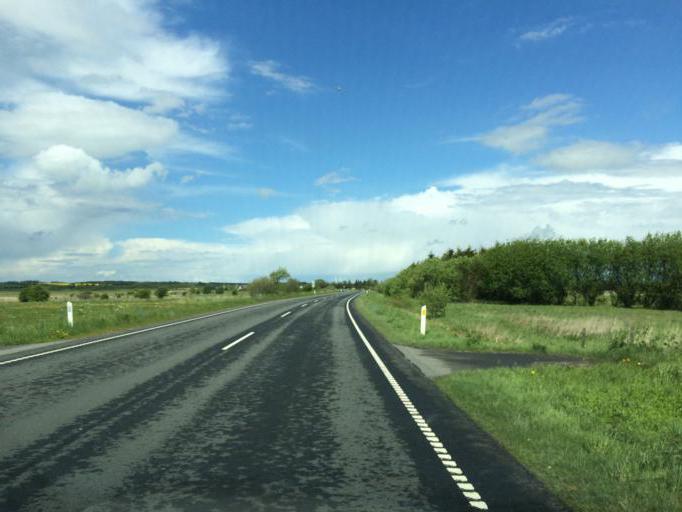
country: DK
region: North Denmark
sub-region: Vesthimmerland Kommune
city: Farso
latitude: 56.6899
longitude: 9.3178
